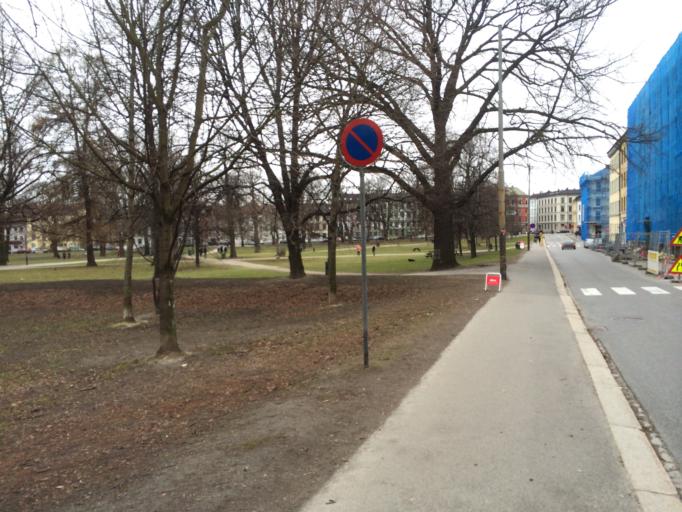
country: NO
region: Oslo
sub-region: Oslo
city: Oslo
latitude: 59.9237
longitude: 10.7649
